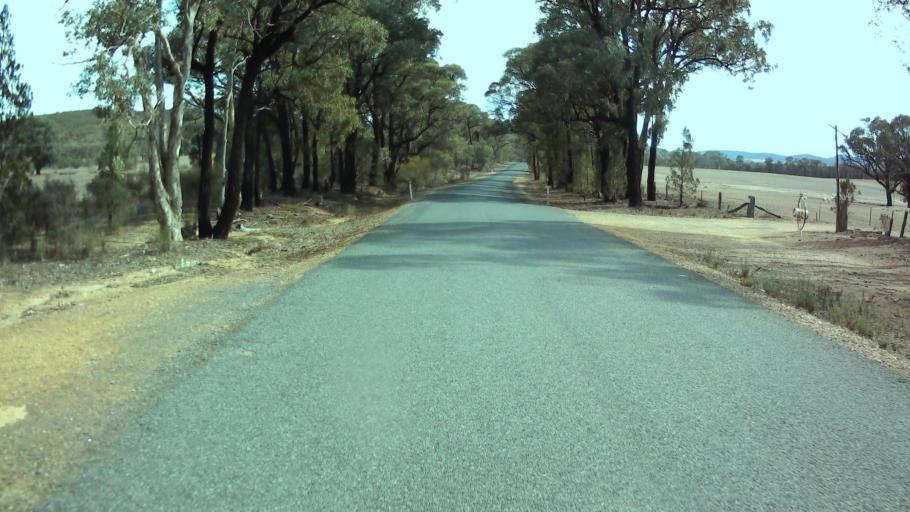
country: AU
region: New South Wales
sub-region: Weddin
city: Grenfell
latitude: -33.8767
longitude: 148.2013
